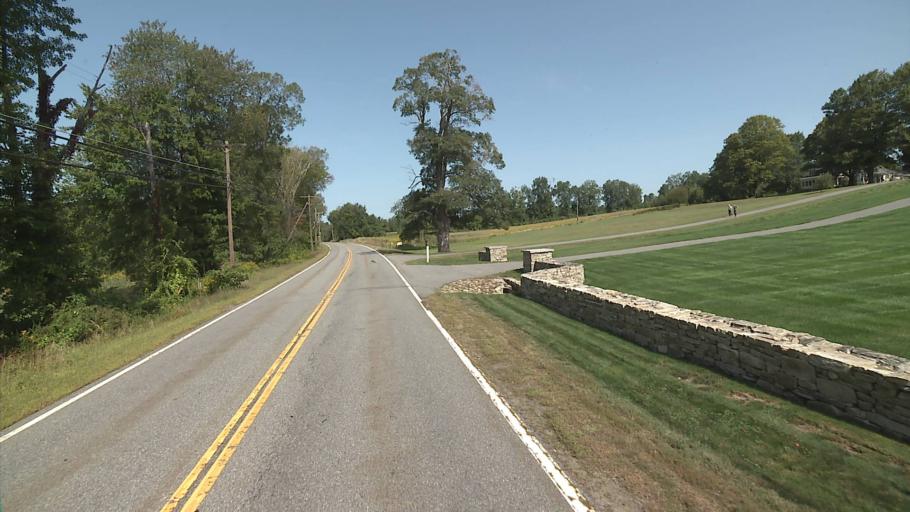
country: US
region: Connecticut
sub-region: Windham County
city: South Woodstock
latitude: 41.9600
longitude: -71.9826
